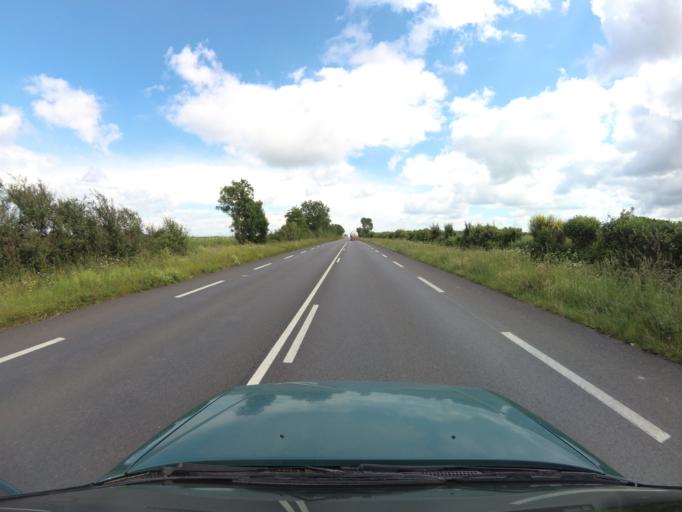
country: FR
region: Pays de la Loire
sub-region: Departement de la Vendee
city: Vendrennes
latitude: 46.8239
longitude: -1.1519
